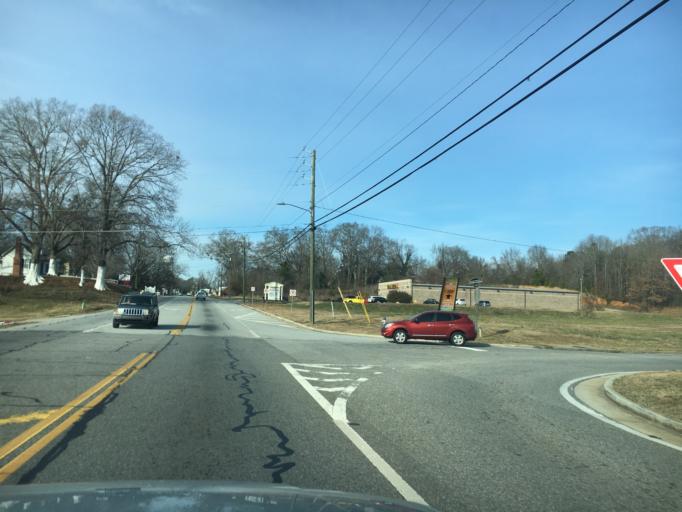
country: US
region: Georgia
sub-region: Jackson County
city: Hoschton
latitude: 34.0929
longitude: -83.7597
